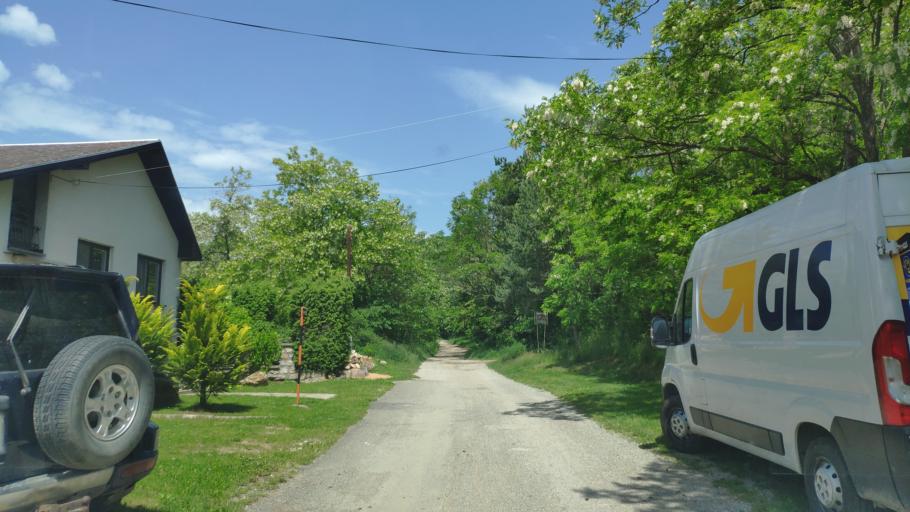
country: SK
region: Kosicky
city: Medzev
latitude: 48.7183
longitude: 20.9702
